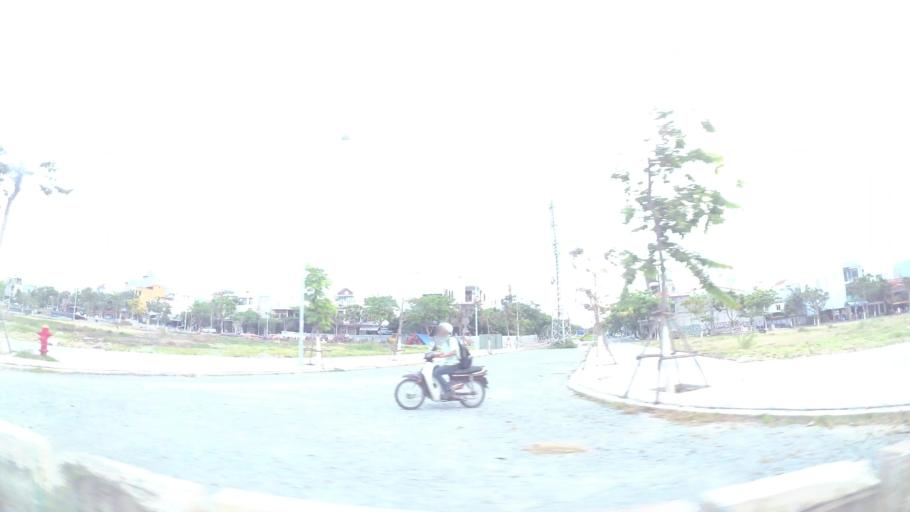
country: VN
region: Da Nang
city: Son Tra
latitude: 16.0511
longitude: 108.2352
